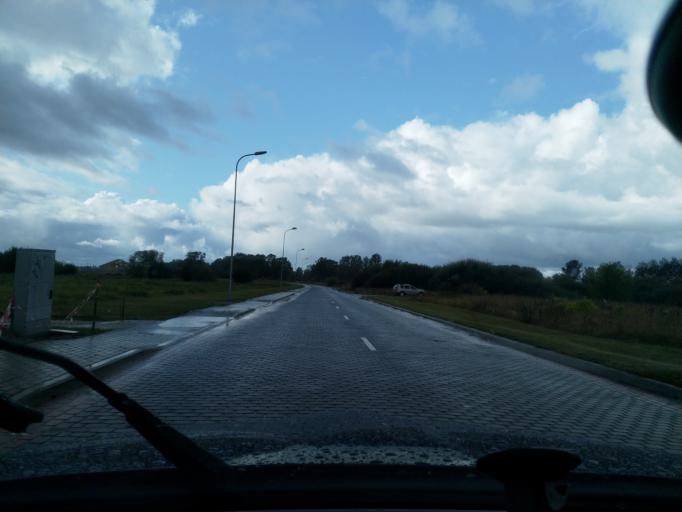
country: LV
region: Ventspils
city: Ventspils
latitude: 57.3703
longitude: 21.5837
